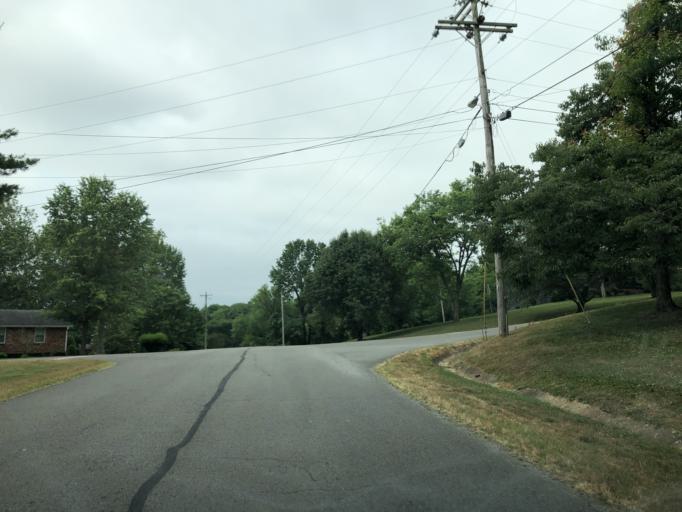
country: US
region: Tennessee
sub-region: Davidson County
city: Goodlettsville
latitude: 36.2863
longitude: -86.7348
